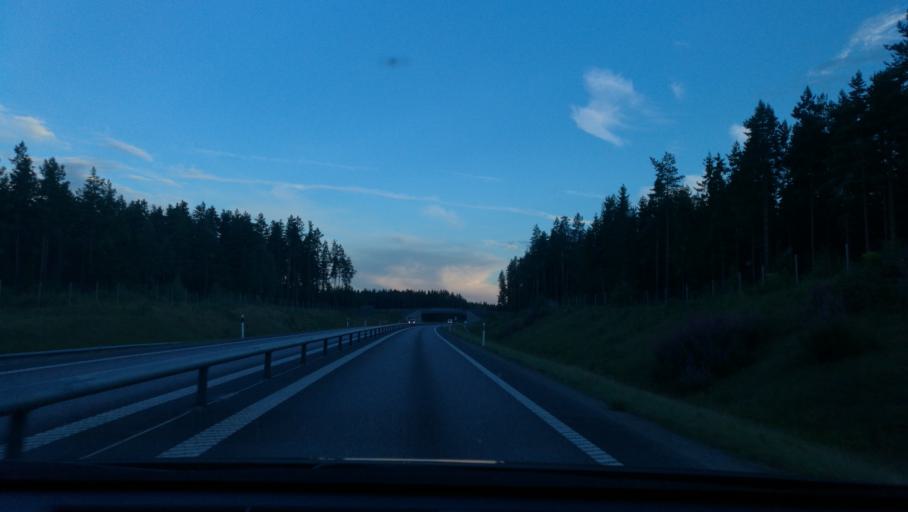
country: SE
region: Soedermanland
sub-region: Katrineholms Kommun
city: Katrineholm
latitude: 58.9885
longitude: 16.2642
